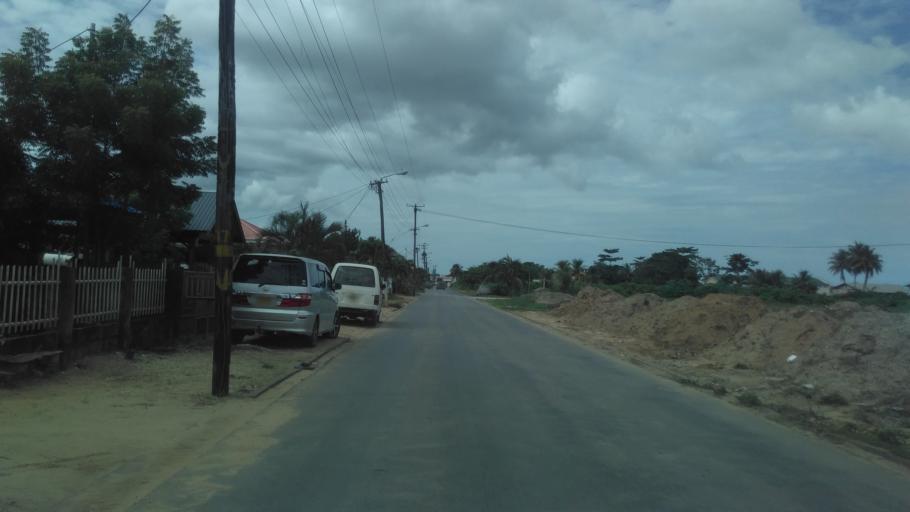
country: SR
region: Paramaribo
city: Paramaribo
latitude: 5.8476
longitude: -55.1248
